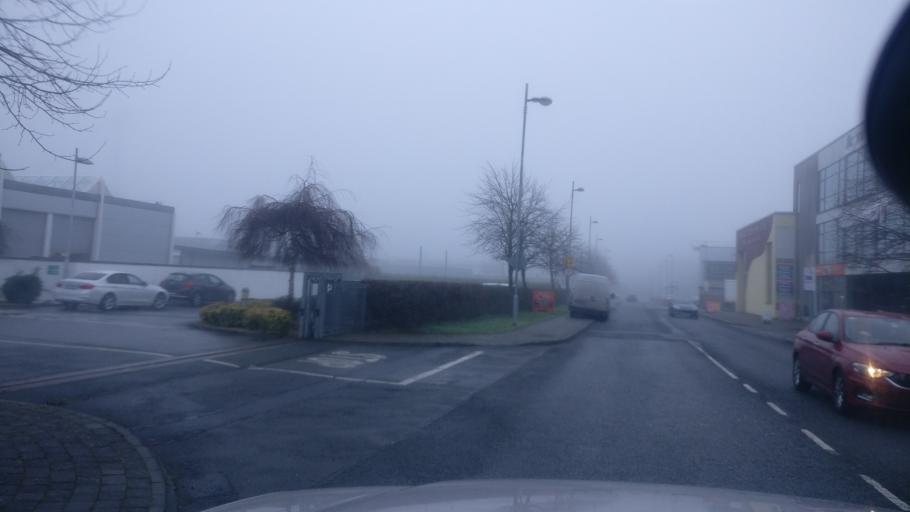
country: IE
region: Munster
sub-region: County Limerick
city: Annacotty
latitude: 52.6496
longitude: -8.5775
